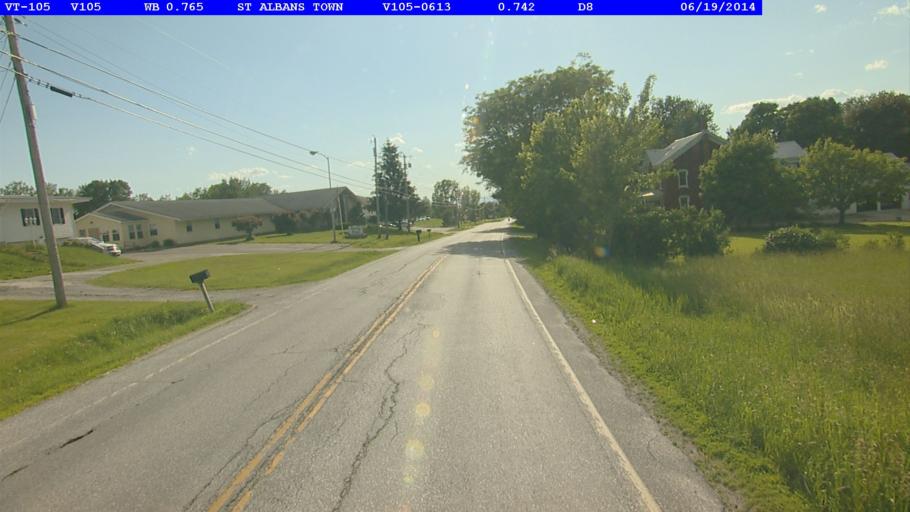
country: US
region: Vermont
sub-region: Franklin County
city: Saint Albans
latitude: 44.8272
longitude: -73.0678
